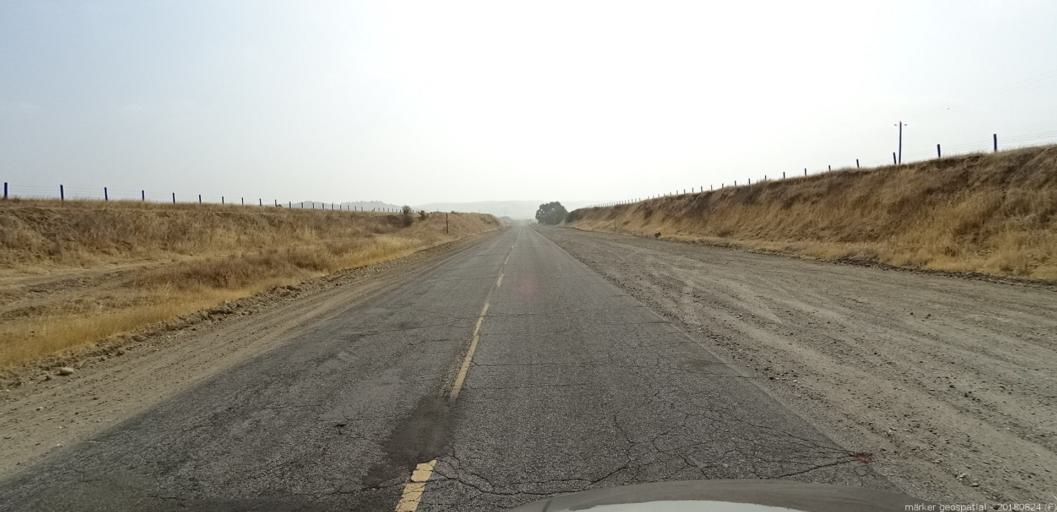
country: US
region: California
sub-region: San Luis Obispo County
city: San Miguel
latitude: 35.8622
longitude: -120.7939
